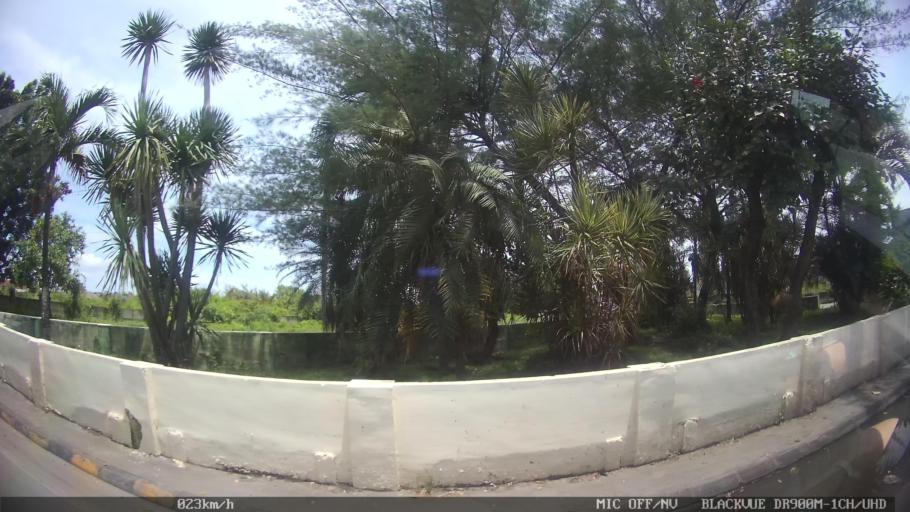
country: ID
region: North Sumatra
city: Belawan
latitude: 3.7717
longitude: 98.6833
